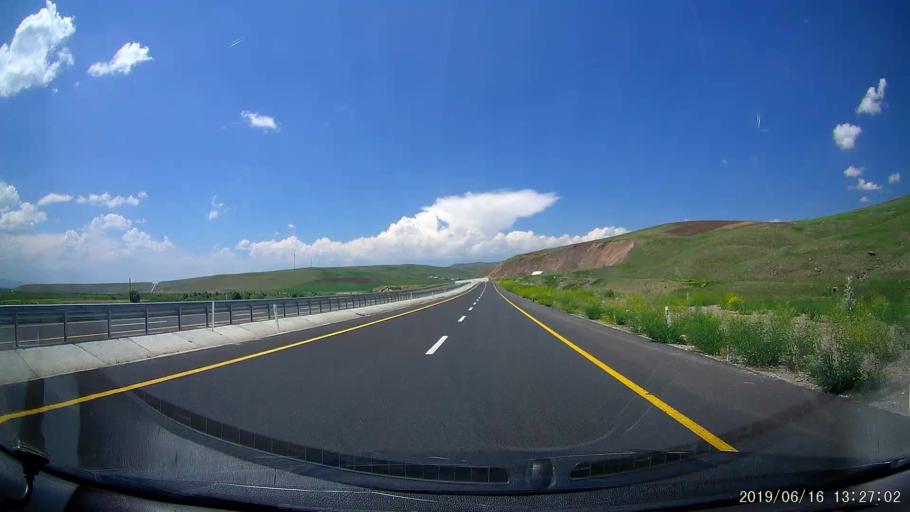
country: TR
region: Agri
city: Taslicay
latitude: 39.6656
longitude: 43.3170
